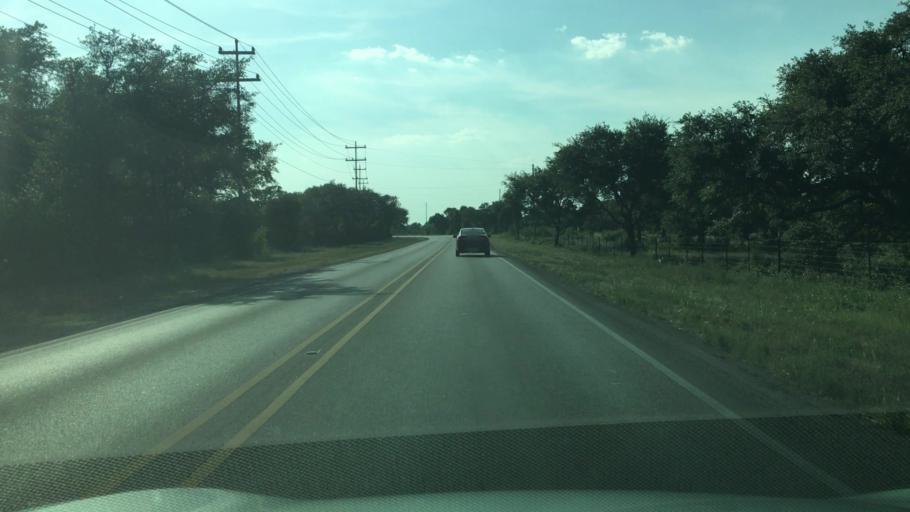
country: US
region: Texas
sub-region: Travis County
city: Shady Hollow
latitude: 30.1158
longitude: -97.9541
